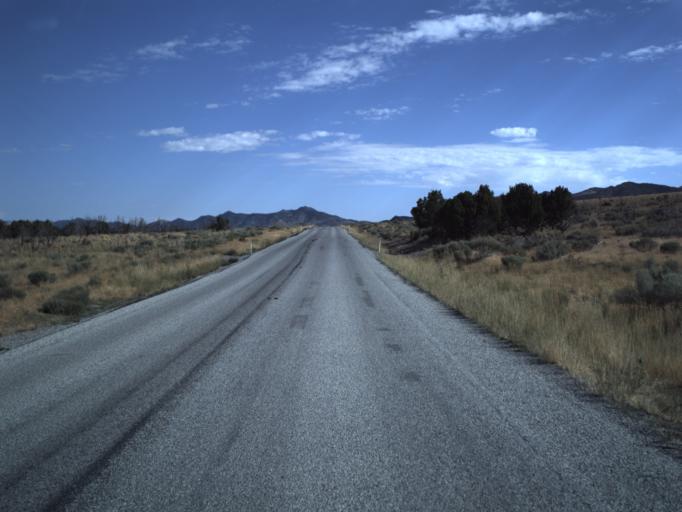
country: US
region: Utah
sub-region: Juab County
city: Mona
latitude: 39.7870
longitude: -112.1500
